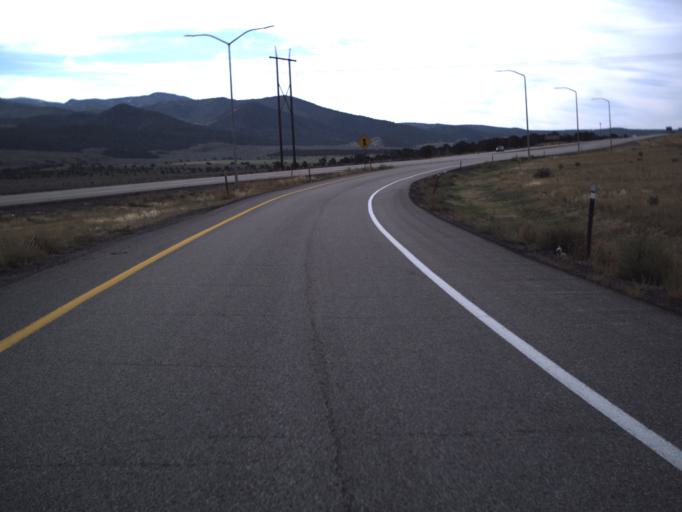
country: US
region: Utah
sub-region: Beaver County
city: Beaver
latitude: 38.5697
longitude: -112.6049
